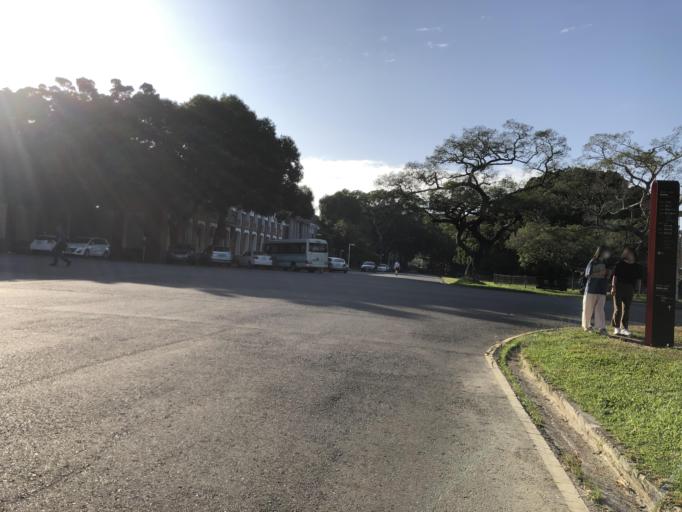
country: TW
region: Taiwan
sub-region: Tainan
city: Tainan
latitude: 22.9999
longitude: 120.2171
